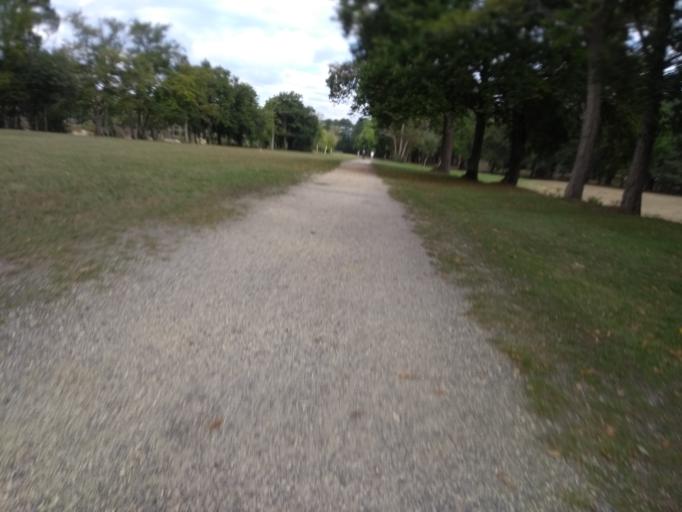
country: FR
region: Aquitaine
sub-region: Departement de la Gironde
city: Saint-Aubin-de-Medoc
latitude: 44.7624
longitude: -0.7009
